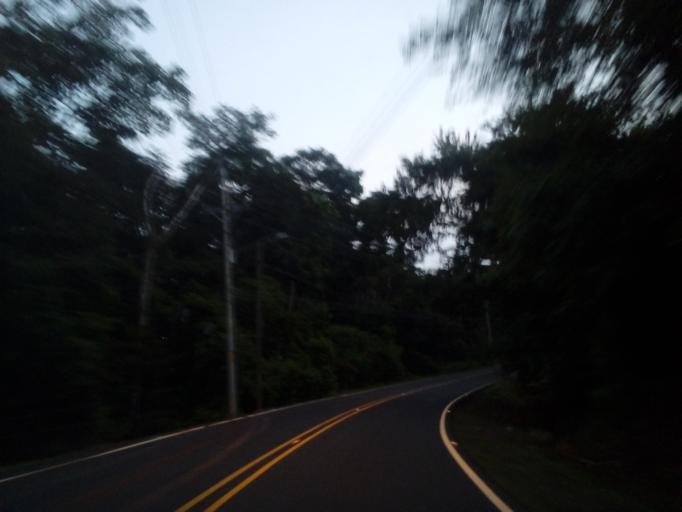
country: CR
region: Guanacaste
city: Samara
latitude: 9.9845
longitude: -85.5038
